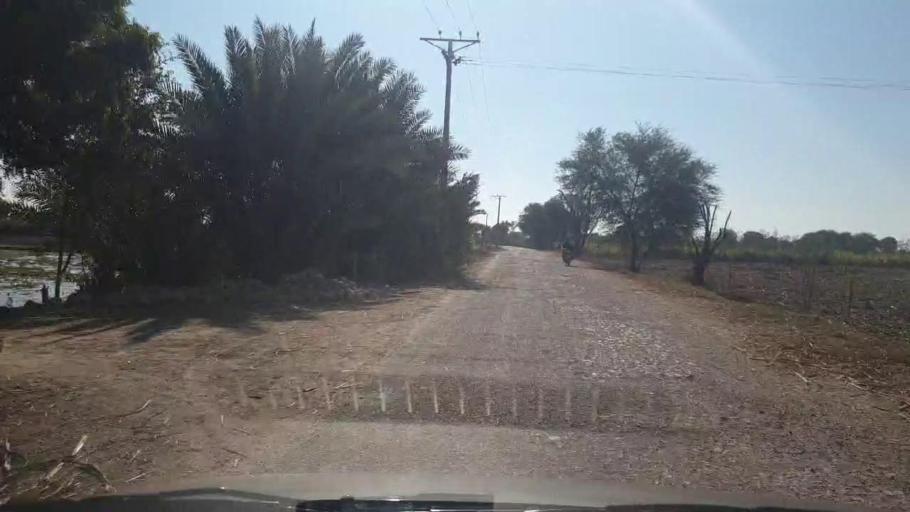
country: PK
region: Sindh
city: Bozdar
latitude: 27.2666
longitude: 68.6520
